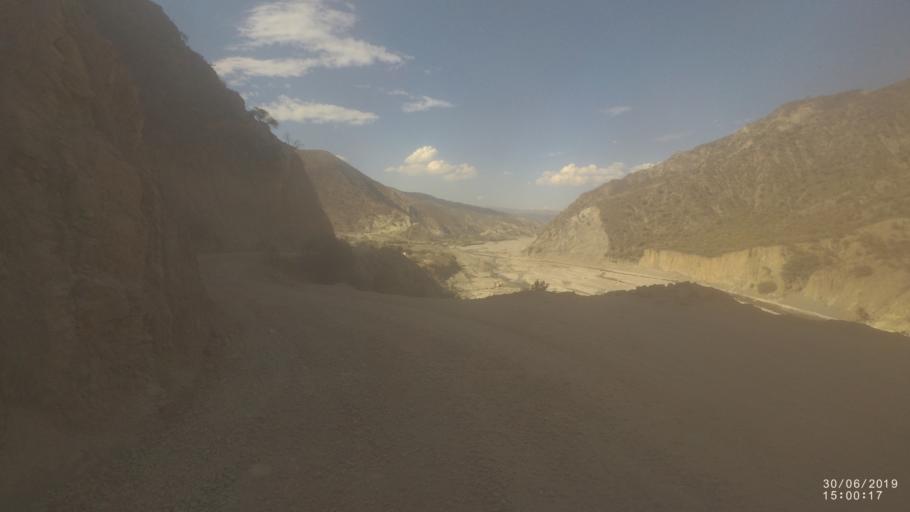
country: BO
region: Cochabamba
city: Irpa Irpa
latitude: -17.7366
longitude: -66.3414
